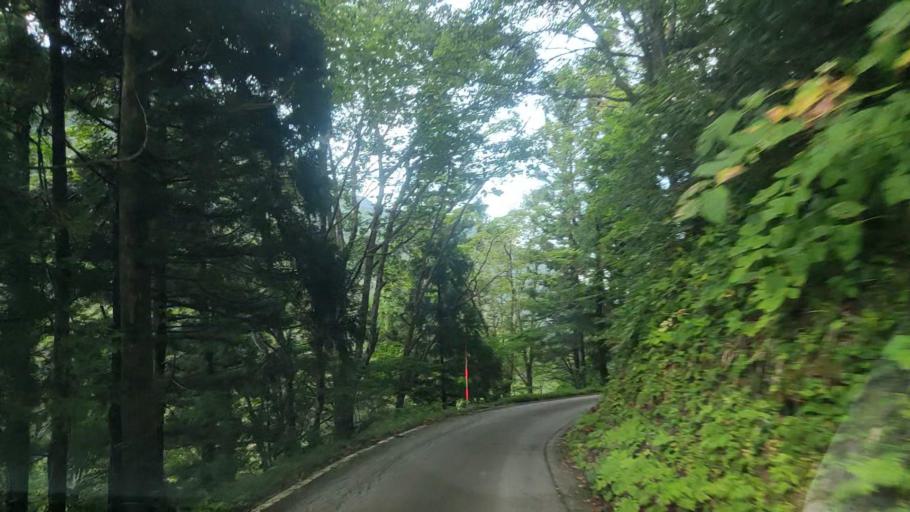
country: JP
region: Toyama
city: Yatsuomachi-higashikumisaka
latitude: 36.4132
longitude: 137.0803
